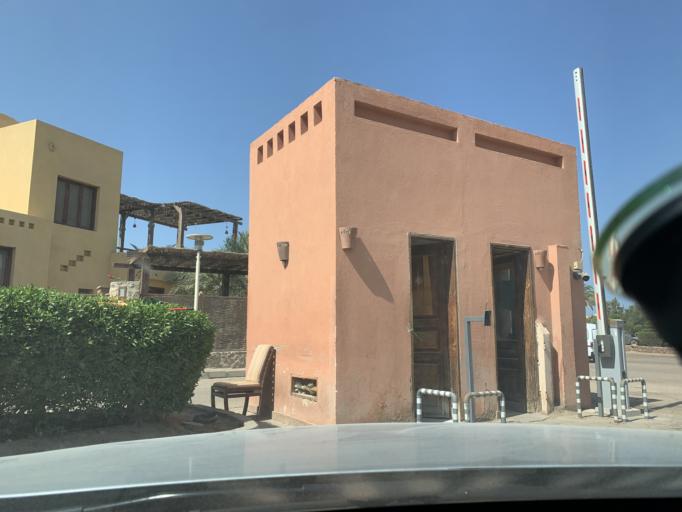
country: EG
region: Red Sea
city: El Gouna
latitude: 27.4029
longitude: 33.6721
